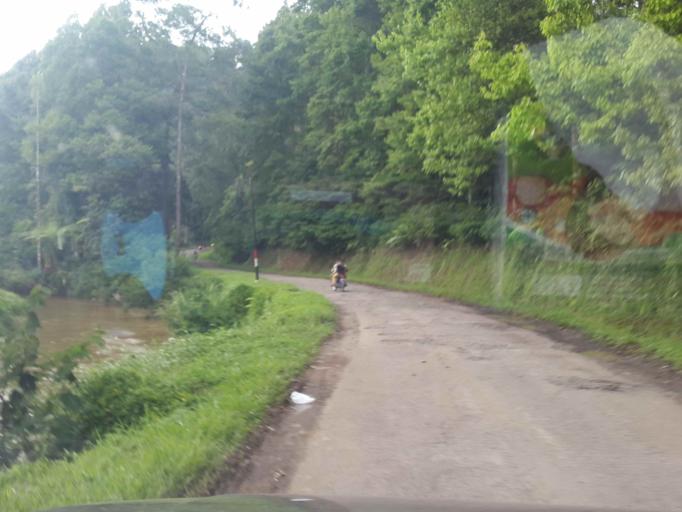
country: ID
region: West Java
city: Ciodeng
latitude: -7.1012
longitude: 107.1104
